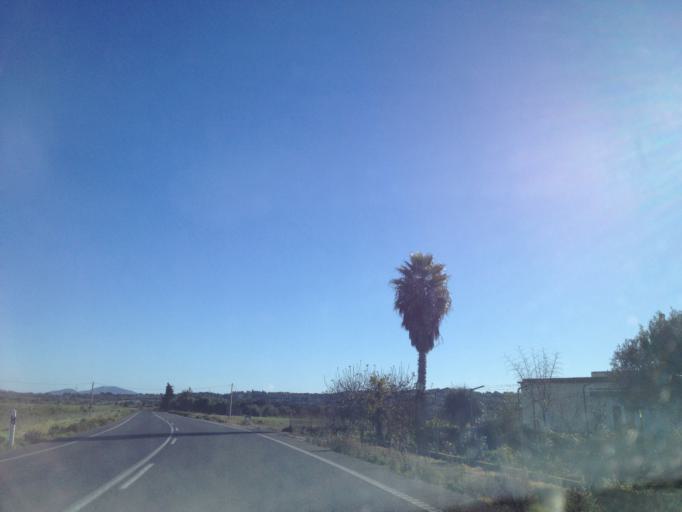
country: ES
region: Balearic Islands
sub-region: Illes Balears
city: Maria de la Salut
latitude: 39.6422
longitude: 3.0621
